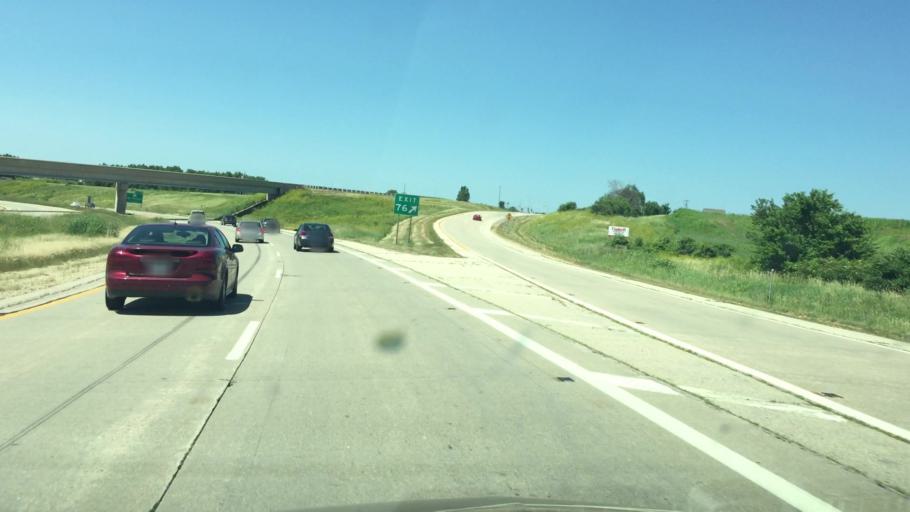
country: US
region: Wisconsin
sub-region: Dane County
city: Verona
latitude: 42.9846
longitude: -89.5563
